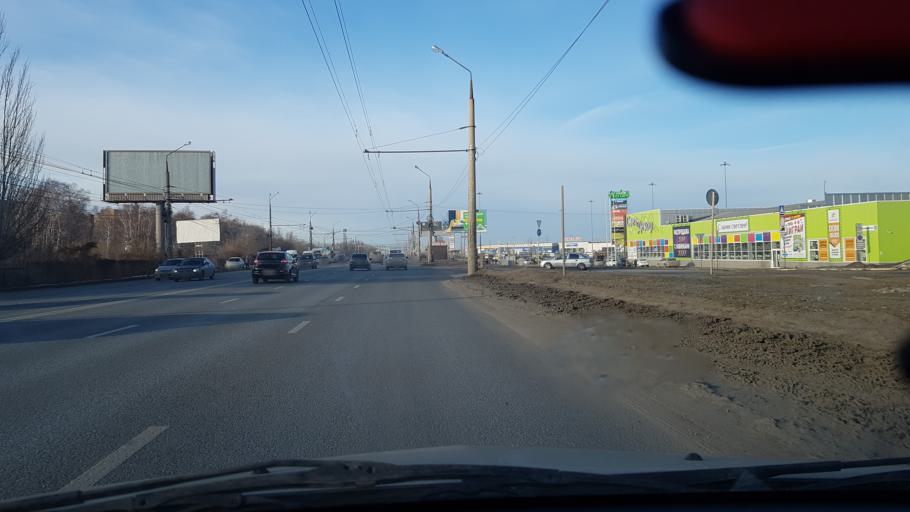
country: RU
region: Samara
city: Tol'yatti
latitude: 53.5383
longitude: 49.3907
